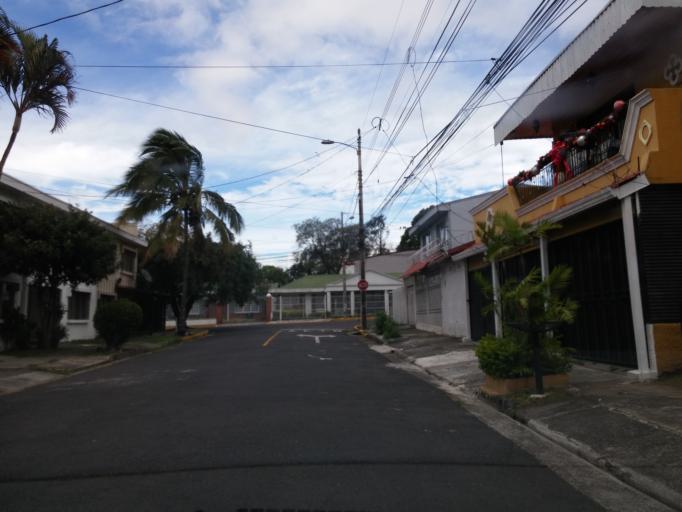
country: CR
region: San Jose
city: San Jose
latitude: 9.9290
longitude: -84.1060
